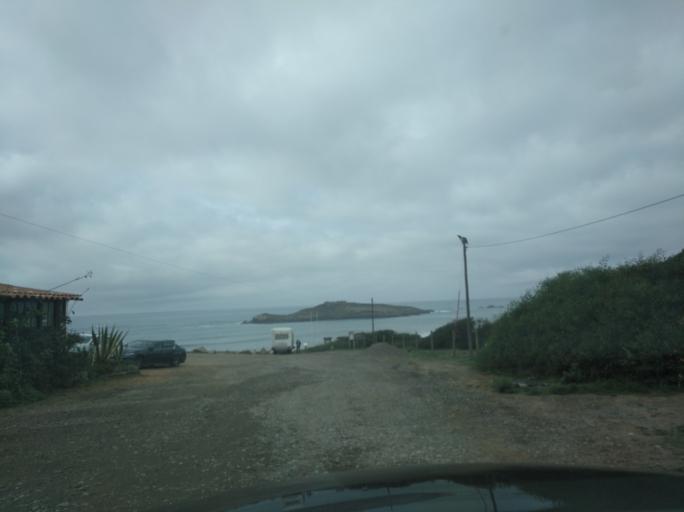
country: PT
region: Setubal
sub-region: Sines
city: Porto Covo
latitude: 37.8289
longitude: -8.7905
